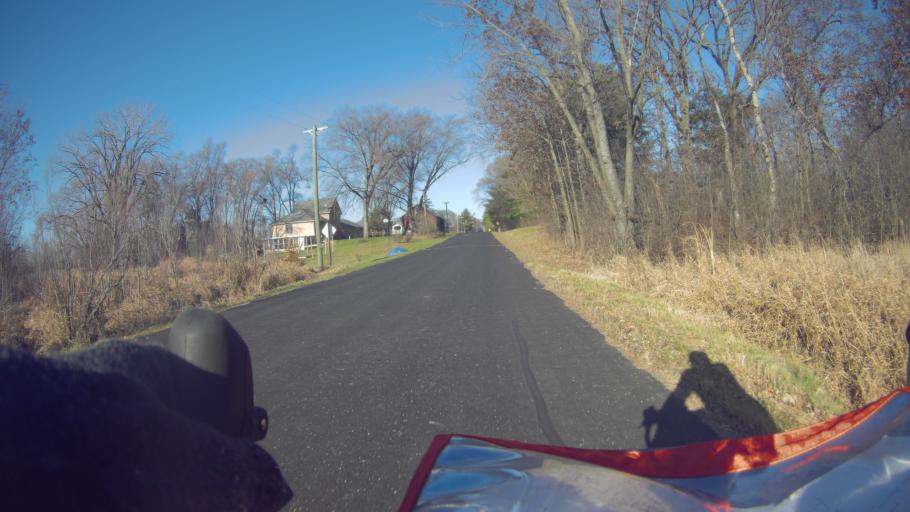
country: US
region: Wisconsin
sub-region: Dane County
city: Stoughton
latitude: 42.8991
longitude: -89.1906
